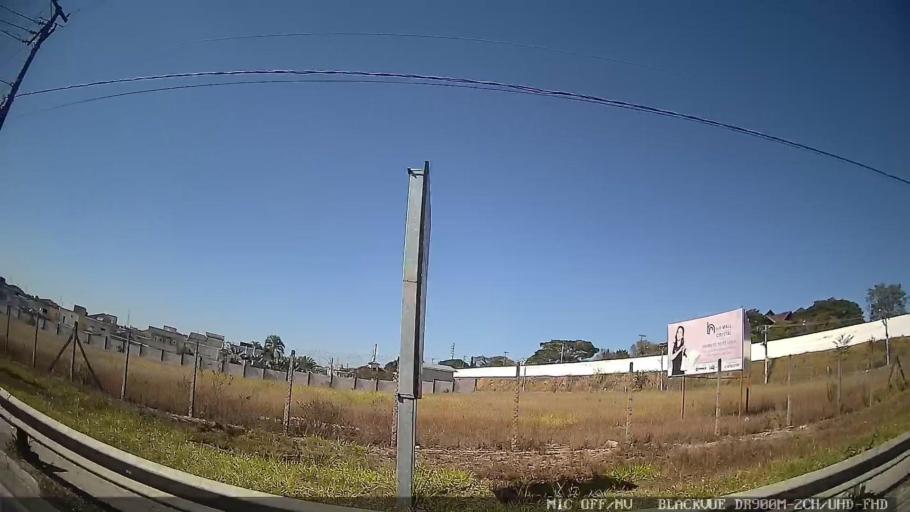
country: BR
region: Sao Paulo
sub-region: Jacarei
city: Jacarei
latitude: -23.2820
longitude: -45.9463
